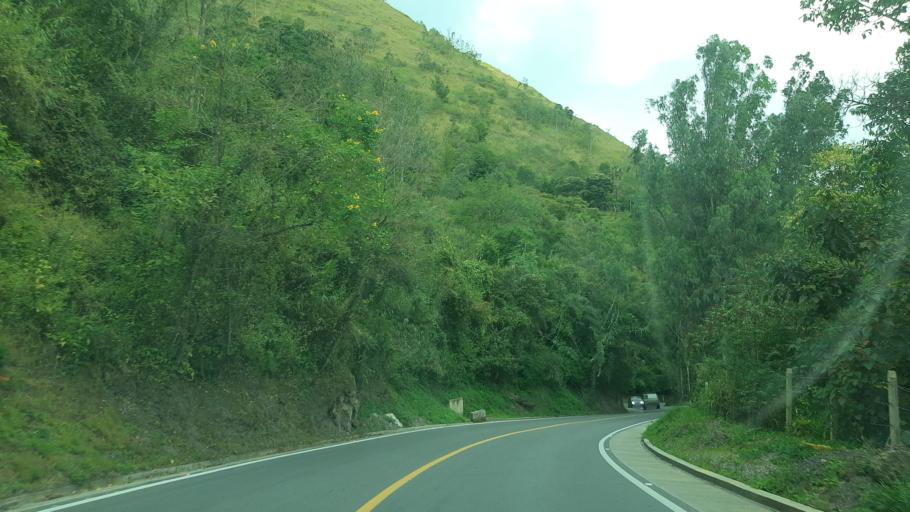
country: CO
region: Boyaca
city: Somondoco
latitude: 5.0104
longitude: -73.4266
